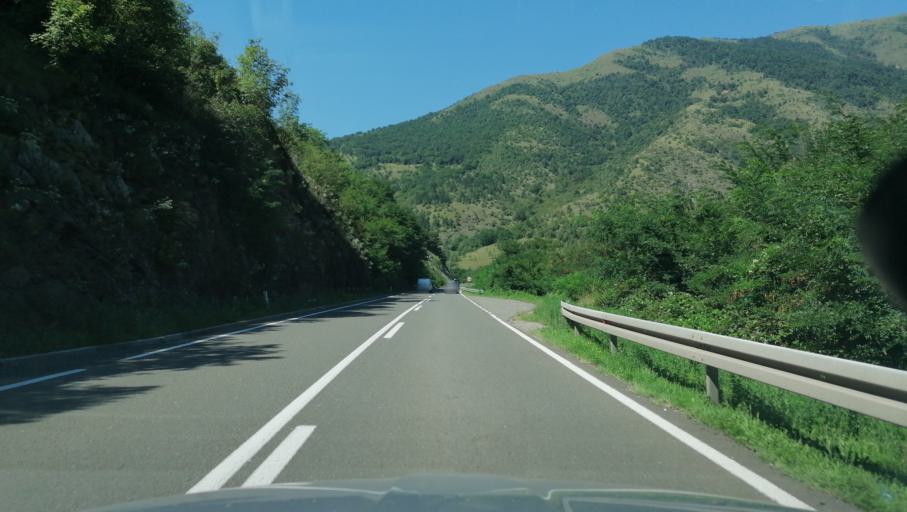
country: RS
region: Central Serbia
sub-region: Raski Okrug
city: Kraljevo
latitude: 43.5918
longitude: 20.5712
